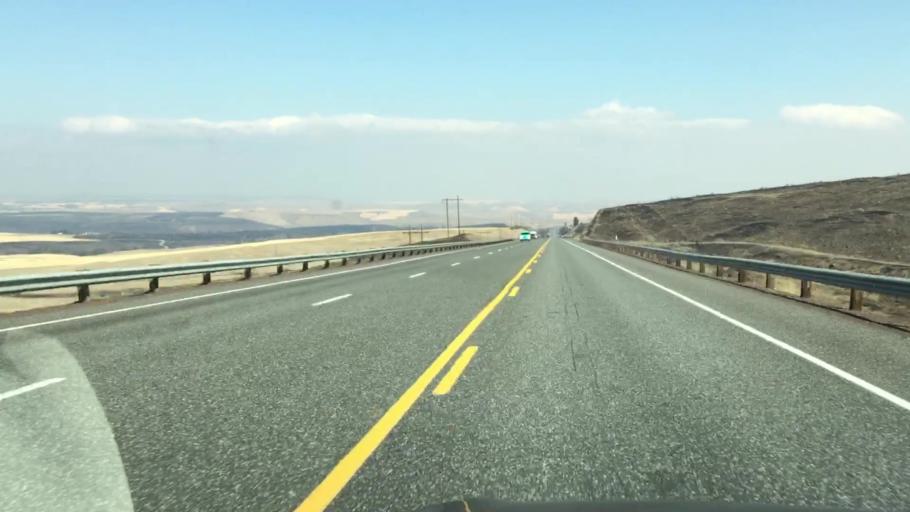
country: US
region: Oregon
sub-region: Wasco County
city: The Dalles
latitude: 45.3674
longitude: -121.1409
